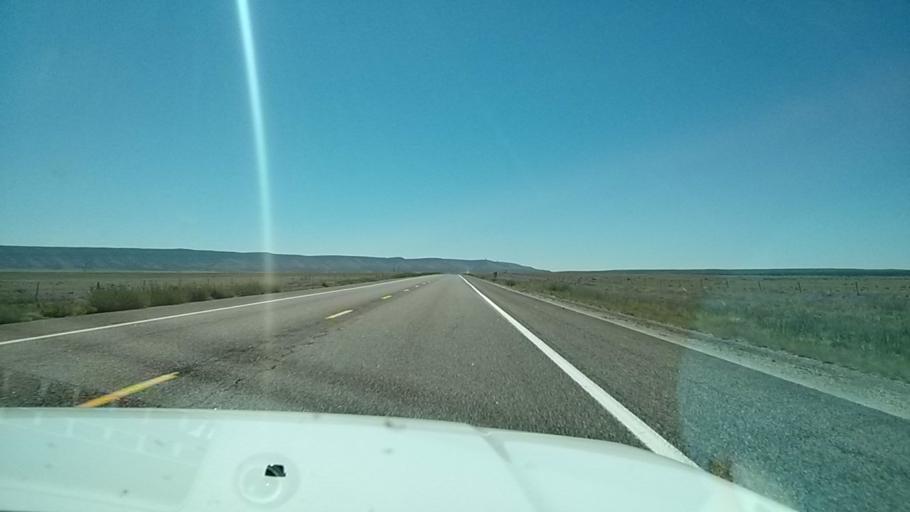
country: US
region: Arizona
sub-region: Mohave County
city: Peach Springs
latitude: 35.4293
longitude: -113.0608
